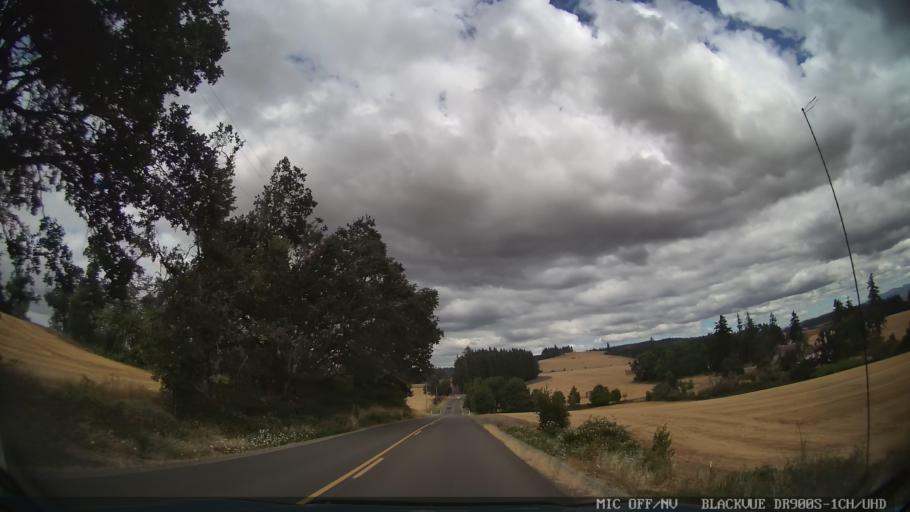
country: US
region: Oregon
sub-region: Marion County
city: Sublimity
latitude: 44.8678
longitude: -122.7504
